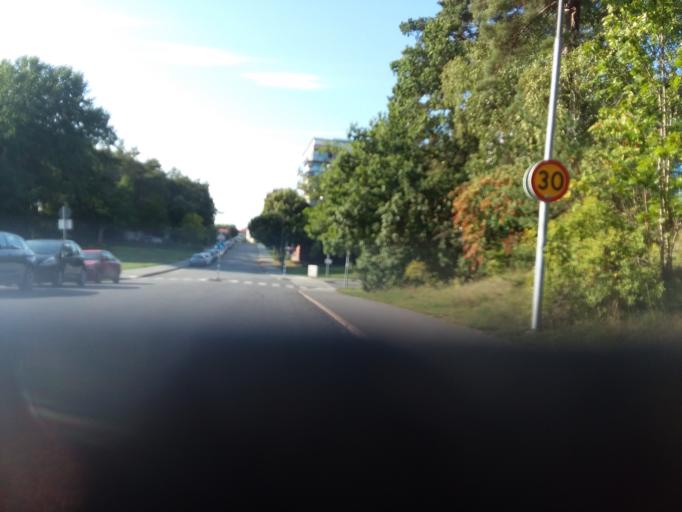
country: SE
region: Stockholm
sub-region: Stockholms Kommun
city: Bromma
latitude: 59.3539
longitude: 17.8771
